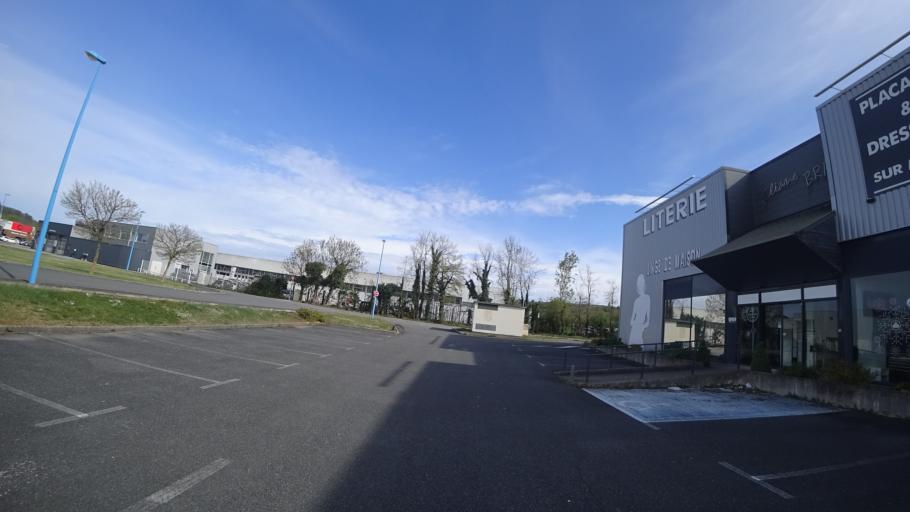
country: FR
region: Midi-Pyrenees
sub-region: Departement de l'Aveyron
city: Sebazac-Concoures
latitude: 44.3763
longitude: 2.5942
